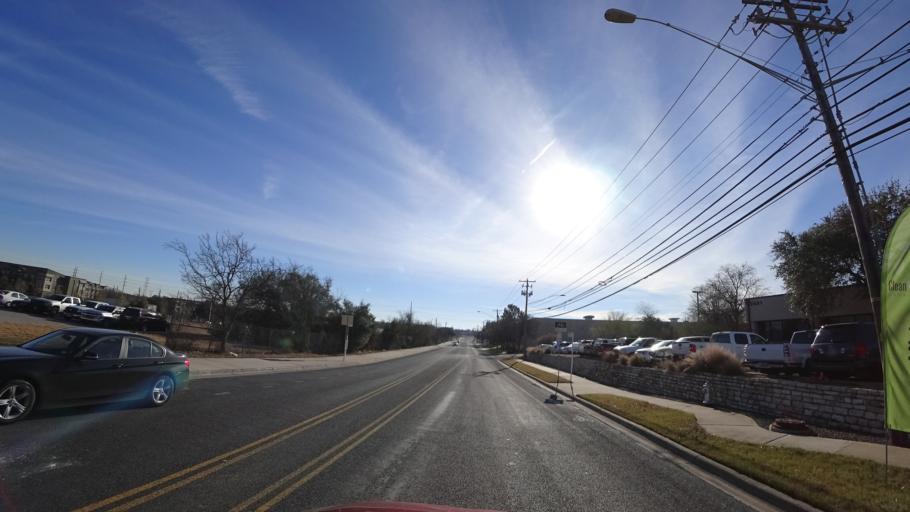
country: US
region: Texas
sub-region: Travis County
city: Wells Branch
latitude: 30.3948
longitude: -97.7196
